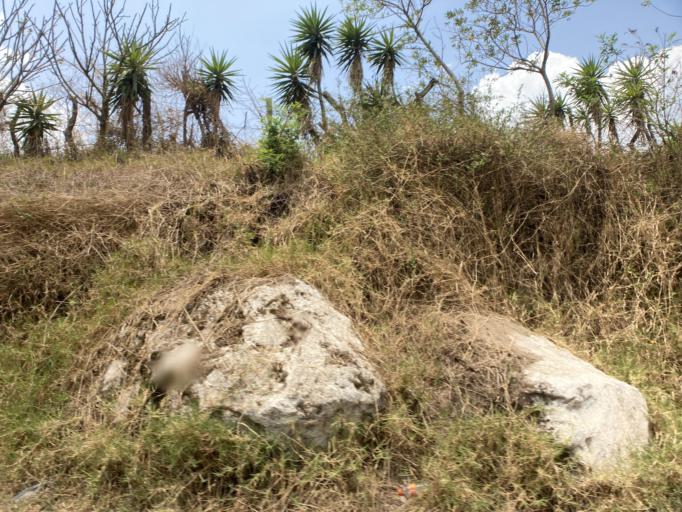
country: GT
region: Escuintla
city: San Vicente Pacaya
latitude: 14.3546
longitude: -90.5722
